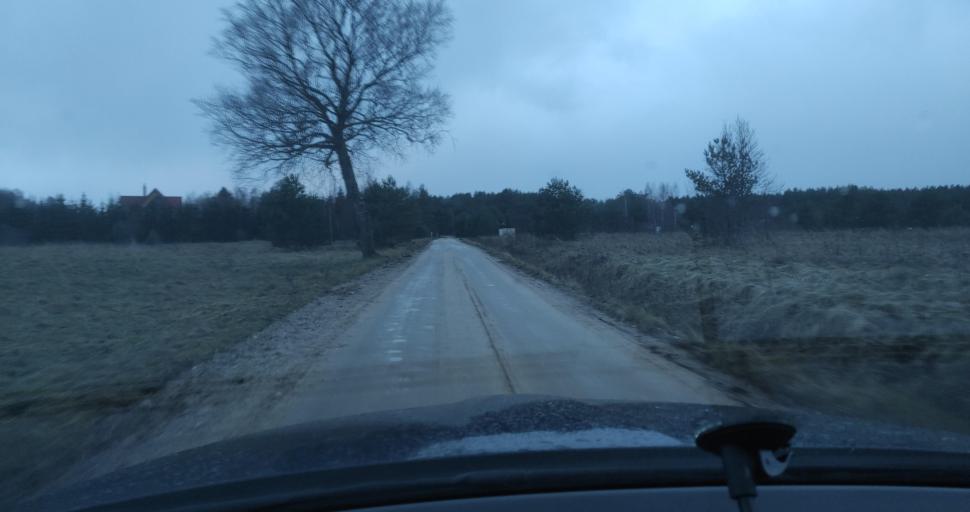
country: LV
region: Pavilostas
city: Pavilosta
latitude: 56.7445
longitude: 21.0716
